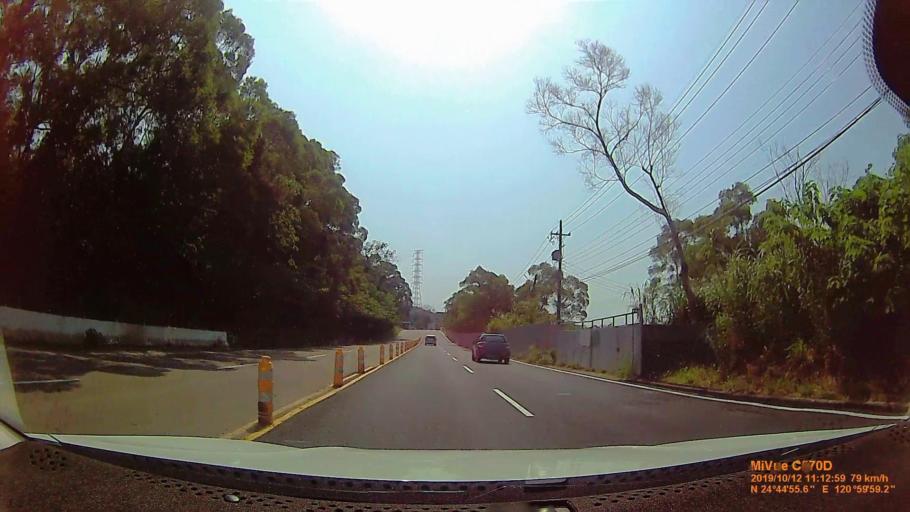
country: TW
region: Taiwan
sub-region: Hsinchu
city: Hsinchu
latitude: 24.7486
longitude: 120.9998
